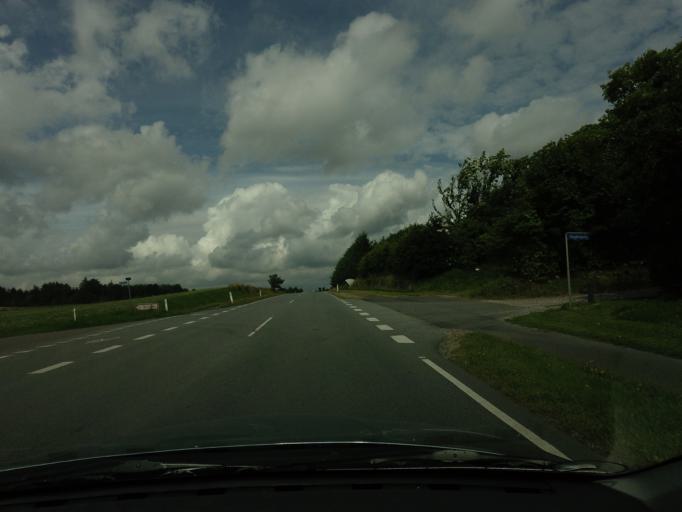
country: DK
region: North Denmark
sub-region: Hjorring Kommune
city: Tars
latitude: 57.3762
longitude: 10.1569
